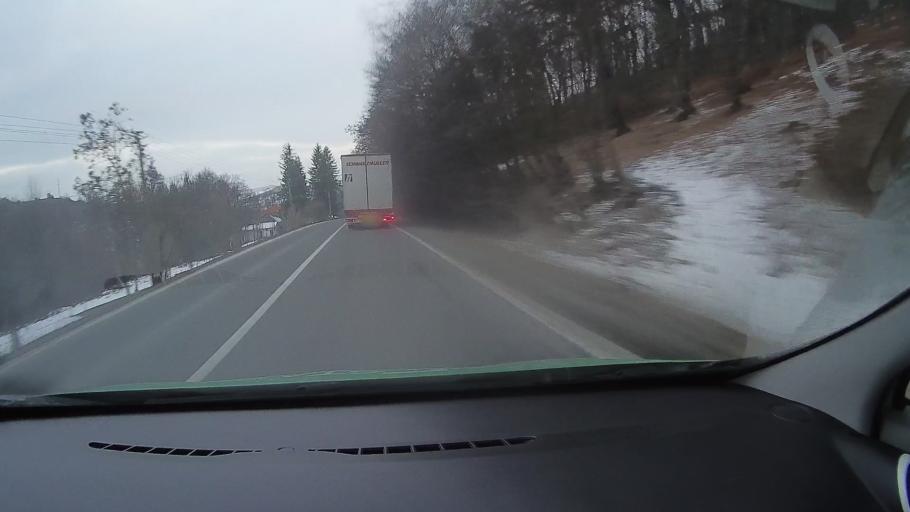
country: RO
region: Harghita
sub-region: Municipiul Odorheiu Secuiesc
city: Odorheiu Secuiesc
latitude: 46.3321
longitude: 25.2727
